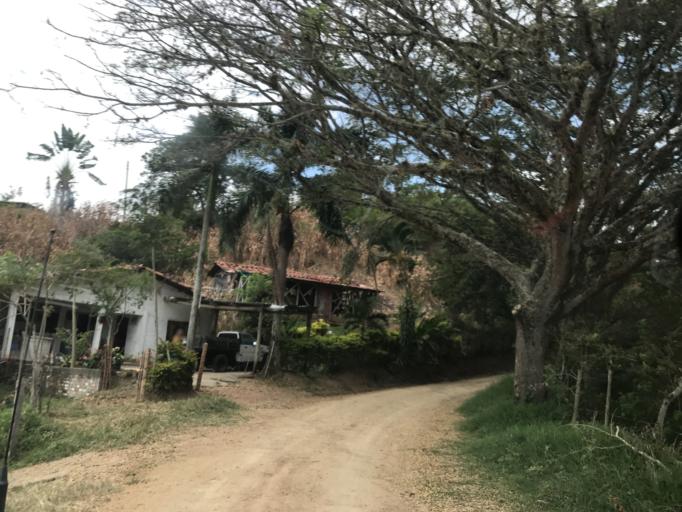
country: CO
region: Valle del Cauca
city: Obando
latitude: 4.5622
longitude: -75.9382
